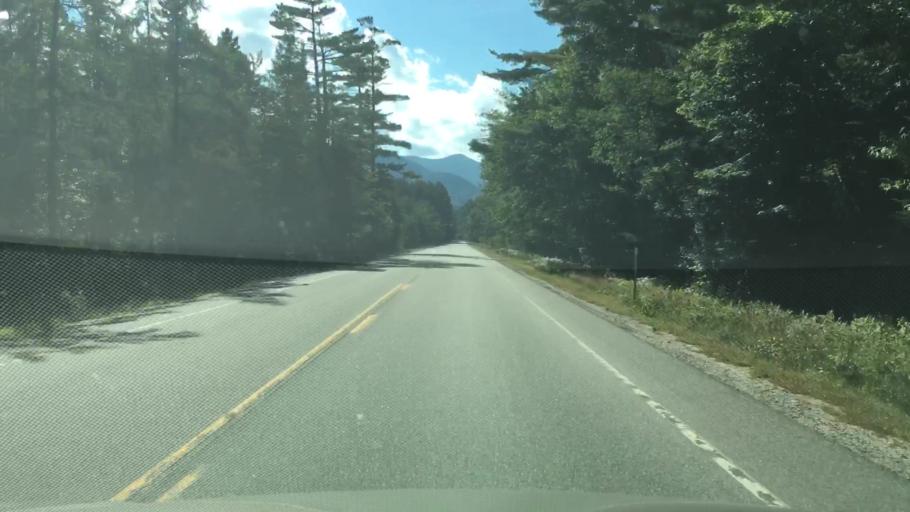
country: US
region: New Hampshire
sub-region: Carroll County
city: Tamworth
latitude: 43.9974
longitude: -71.3593
